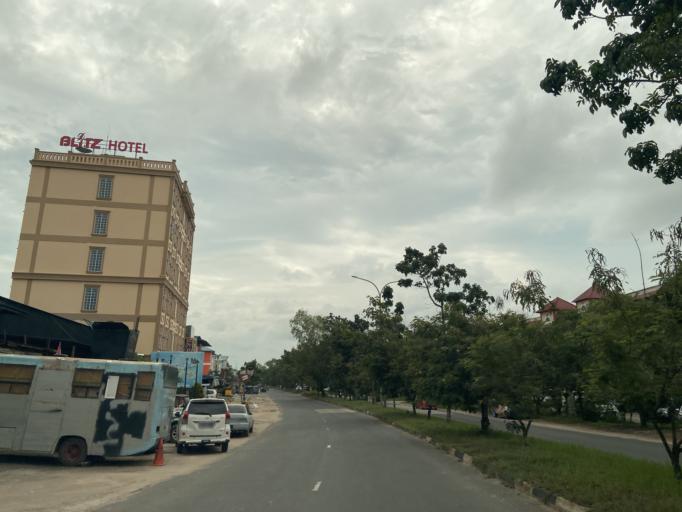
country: SG
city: Singapore
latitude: 1.1228
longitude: 104.0494
